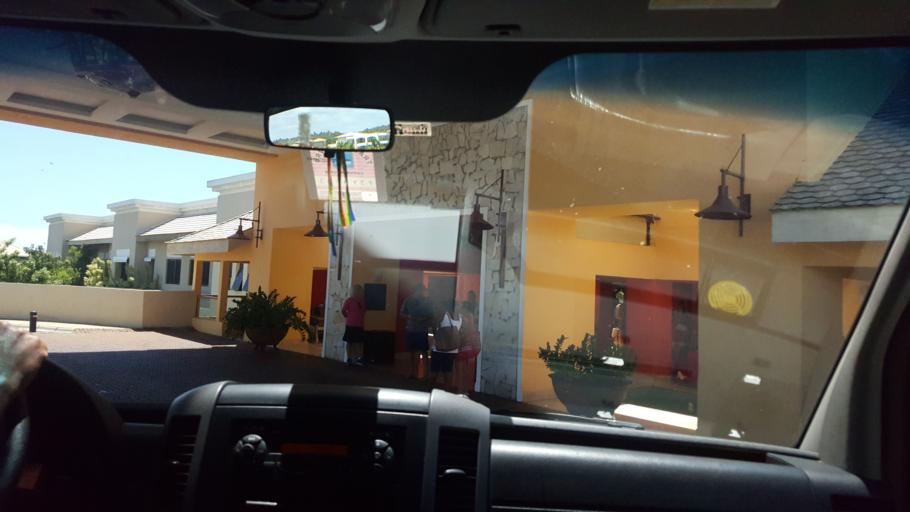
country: BR
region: Bahia
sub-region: Mata De Sao Joao
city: Mata de Sao Joao
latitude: -12.5466
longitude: -37.9873
